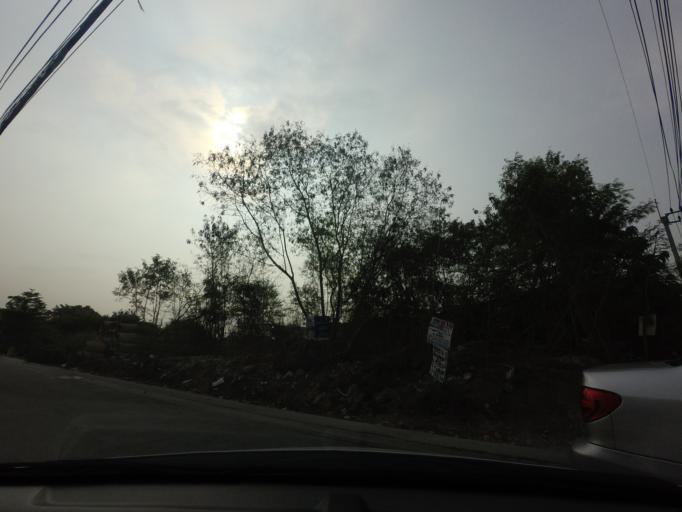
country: TH
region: Bangkok
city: Nong Khaem
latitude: 13.7346
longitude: 100.3553
